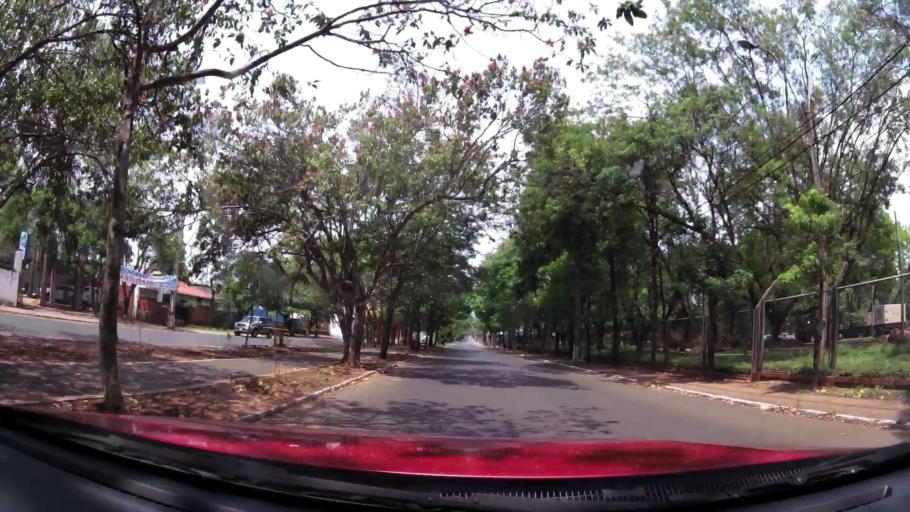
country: PY
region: Central
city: Fernando de la Mora
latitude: -25.3116
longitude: -57.5655
